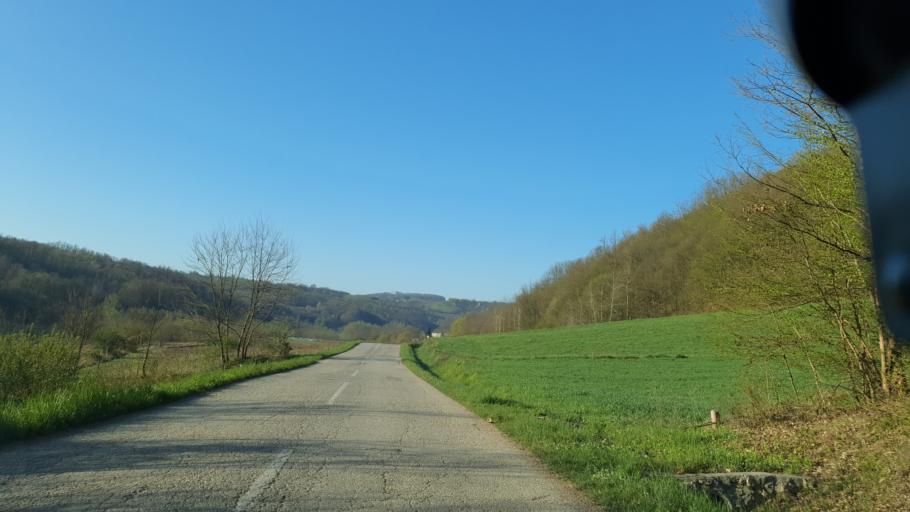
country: RS
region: Central Serbia
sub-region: Kolubarski Okrug
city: Osecina
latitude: 44.3715
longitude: 19.5424
